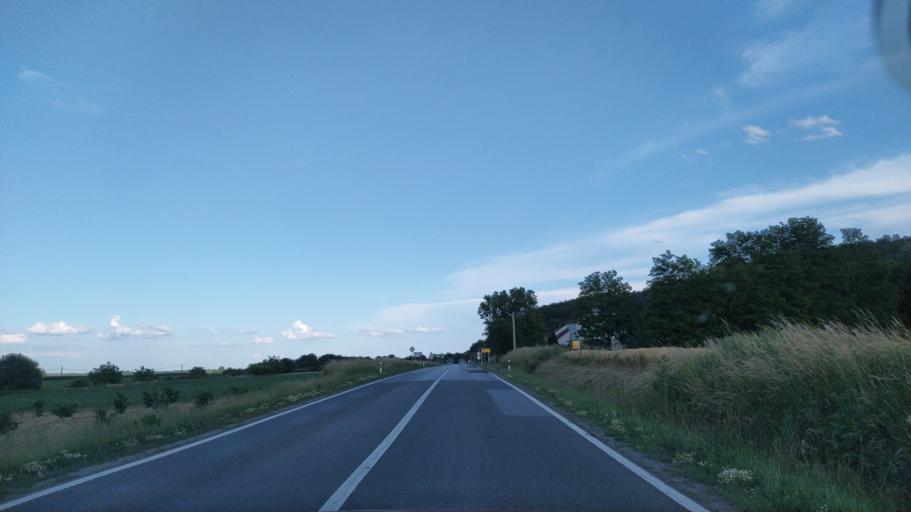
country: HR
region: Virovitick-Podravska
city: Suhopolje
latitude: 45.7469
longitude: 17.5977
